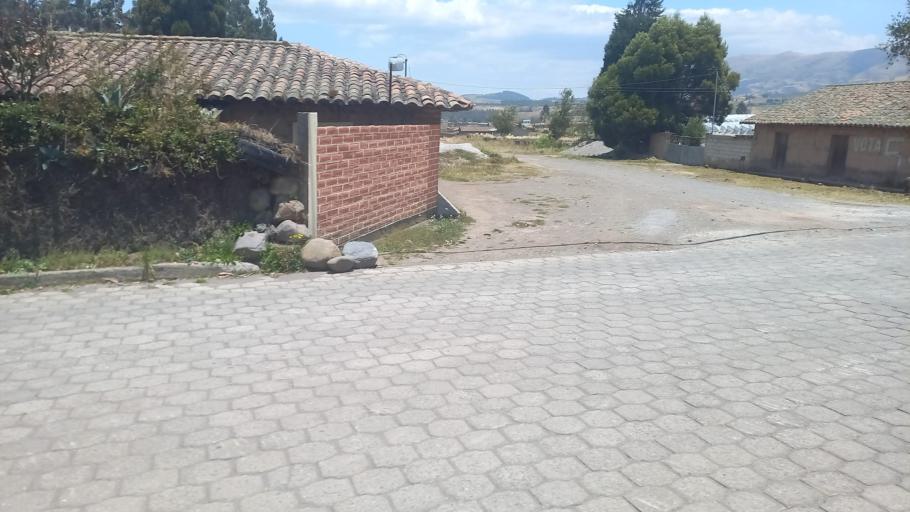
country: EC
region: Pichincha
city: Cayambe
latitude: 0.1400
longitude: -78.0677
